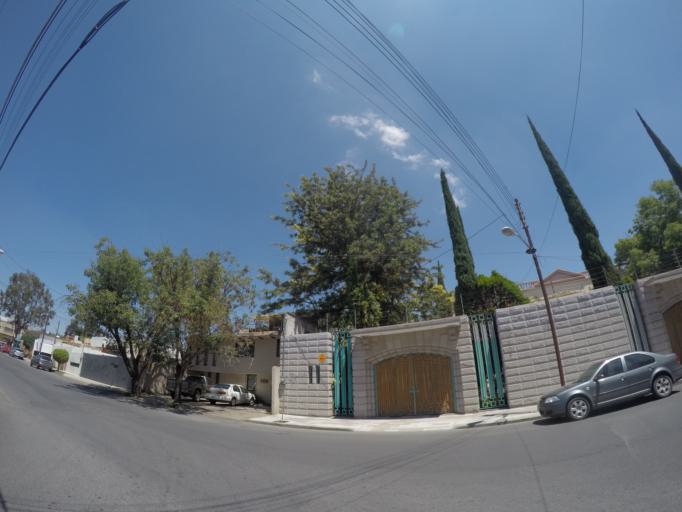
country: MX
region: San Luis Potosi
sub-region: San Luis Potosi
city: San Luis Potosi
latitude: 22.1477
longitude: -101.0064
